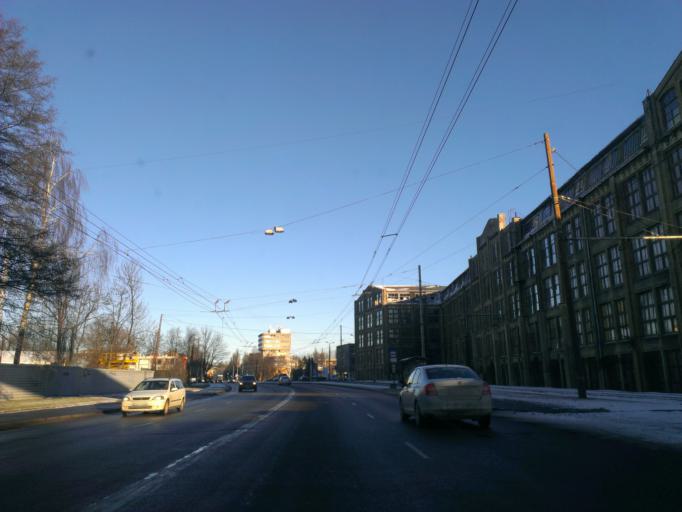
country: LV
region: Riga
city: Riga
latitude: 56.9853
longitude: 24.1205
